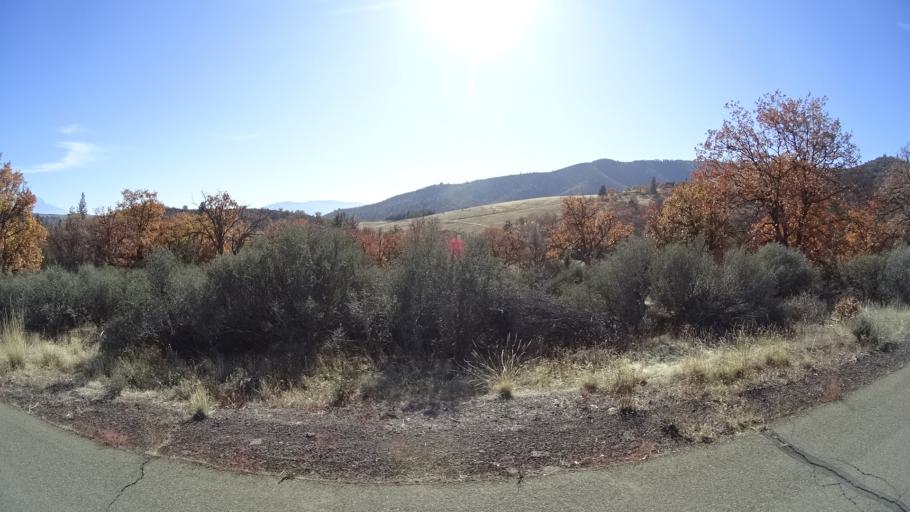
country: US
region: California
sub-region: Siskiyou County
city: Yreka
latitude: 41.7692
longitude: -122.6358
